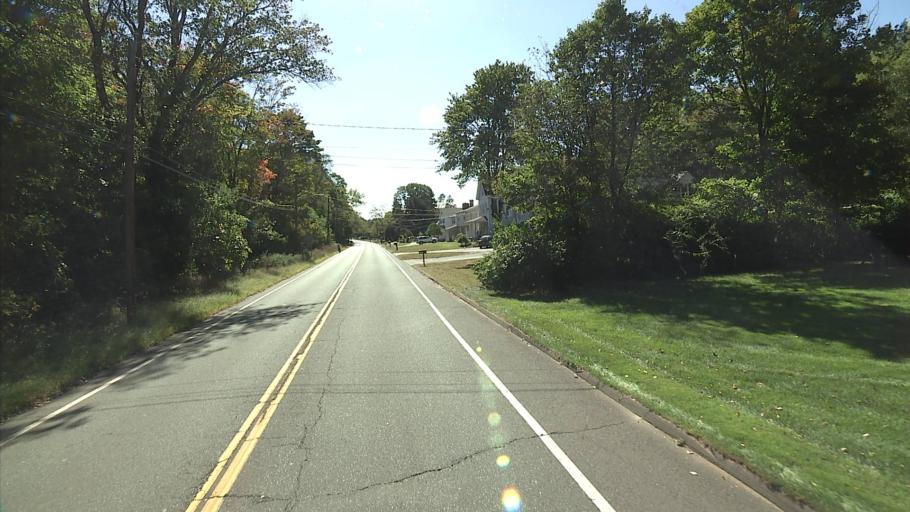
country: US
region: Connecticut
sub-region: New Haven County
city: Woodbridge
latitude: 41.3509
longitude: -72.9841
